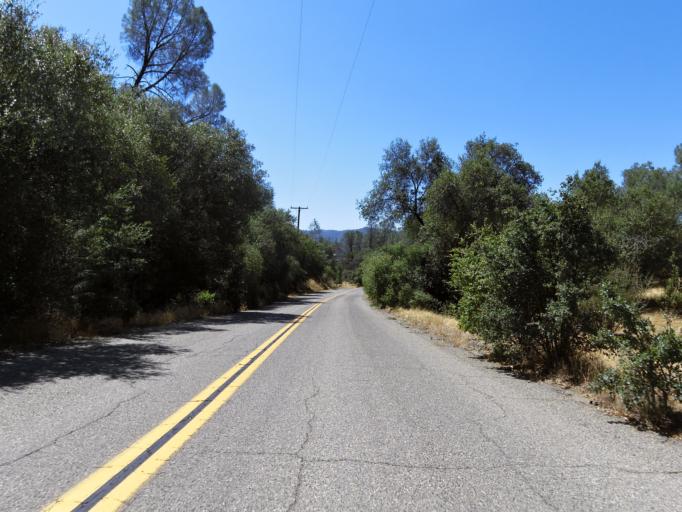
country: US
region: California
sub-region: Fresno County
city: Auberry
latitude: 37.1604
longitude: -119.5157
